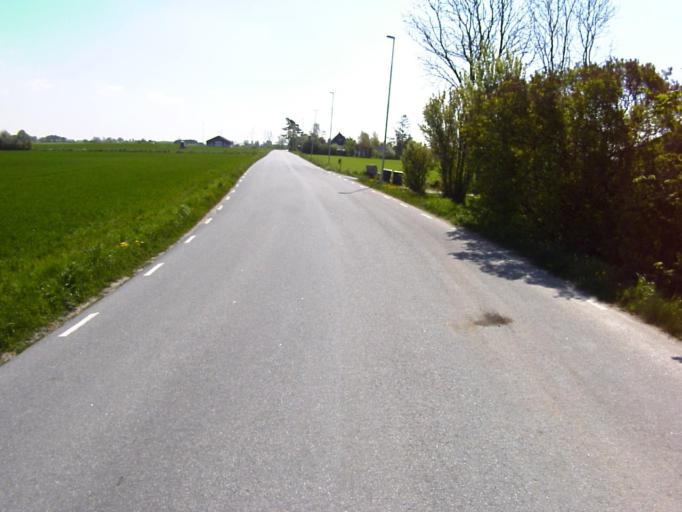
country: SE
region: Skane
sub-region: Kristianstads Kommun
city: Kristianstad
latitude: 56.0212
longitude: 14.2158
